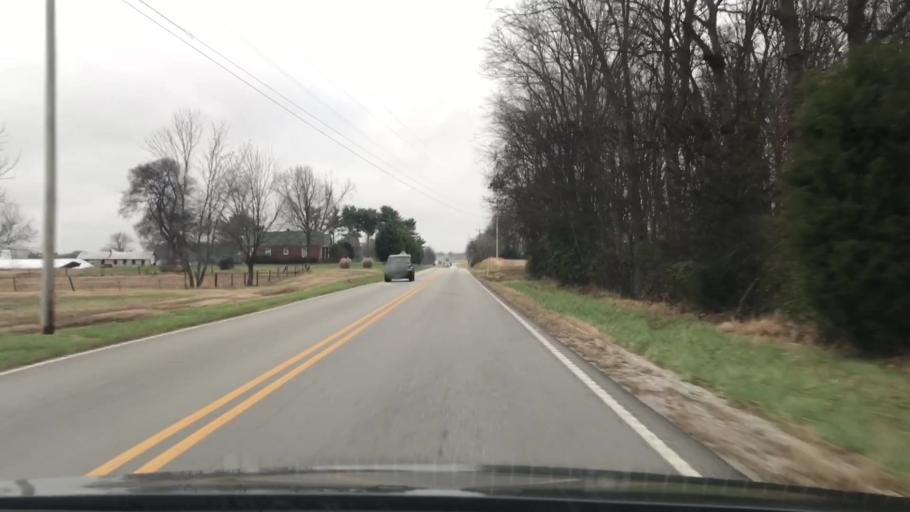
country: US
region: Kentucky
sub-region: Todd County
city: Guthrie
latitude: 36.6939
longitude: -87.2005
